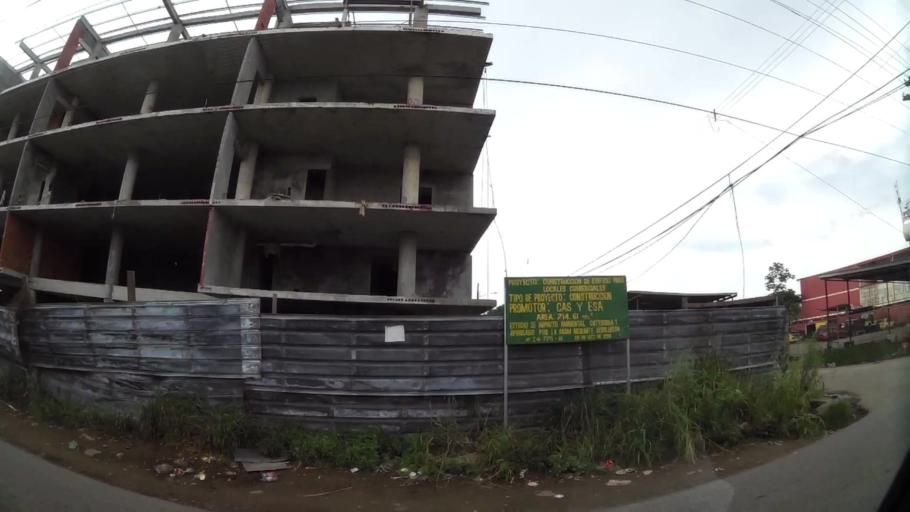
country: PA
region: Panama
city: Tocumen
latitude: 9.1047
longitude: -79.3670
